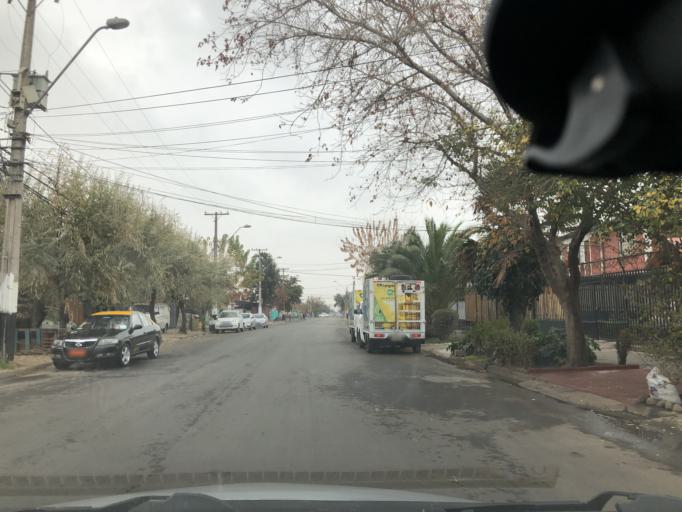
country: CL
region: Santiago Metropolitan
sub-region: Provincia de Cordillera
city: Puente Alto
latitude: -33.5825
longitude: -70.5895
